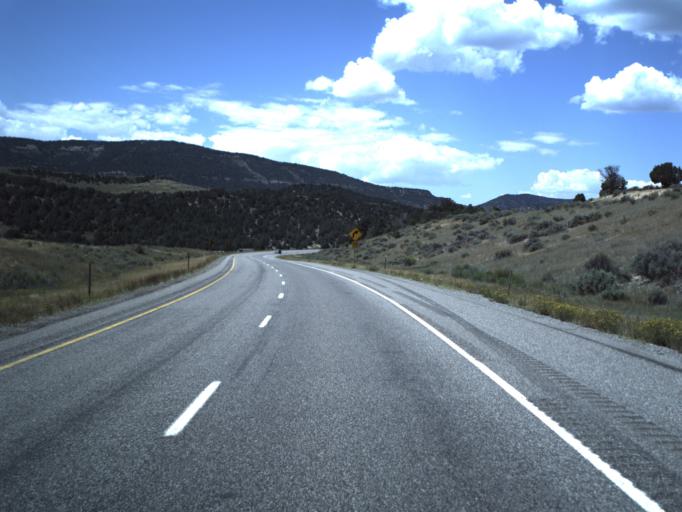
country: US
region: Utah
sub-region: Sevier County
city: Salina
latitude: 38.8510
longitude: -111.5431
